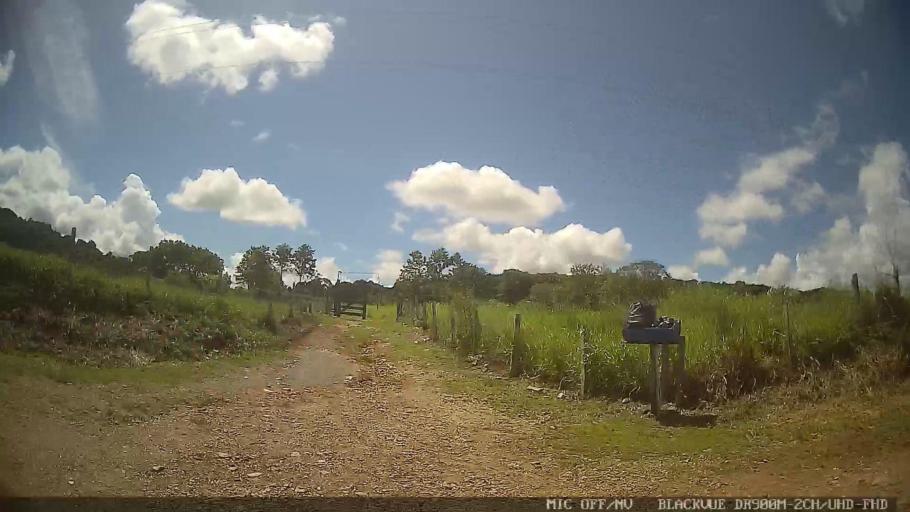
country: BR
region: Sao Paulo
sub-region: Amparo
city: Amparo
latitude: -22.8232
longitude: -46.6990
